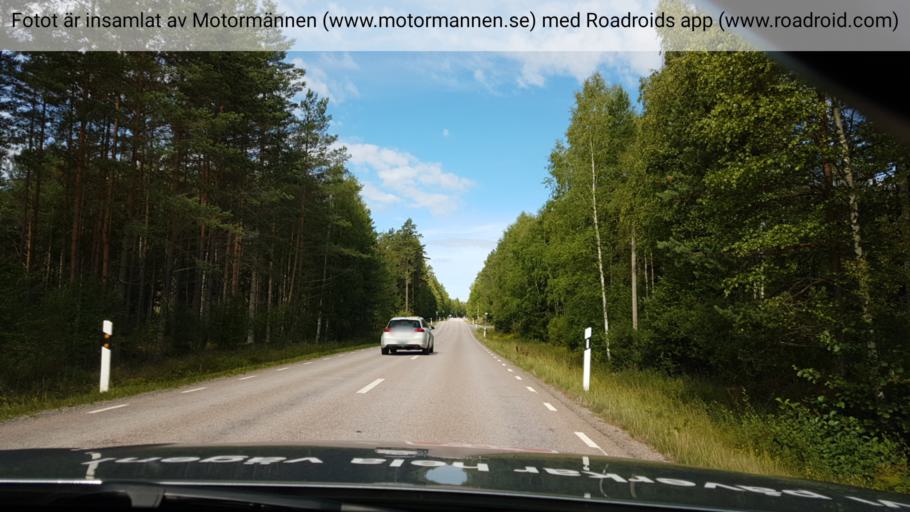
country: SE
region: Uppsala
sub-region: Heby Kommun
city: OEstervala
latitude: 60.0363
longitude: 17.2540
